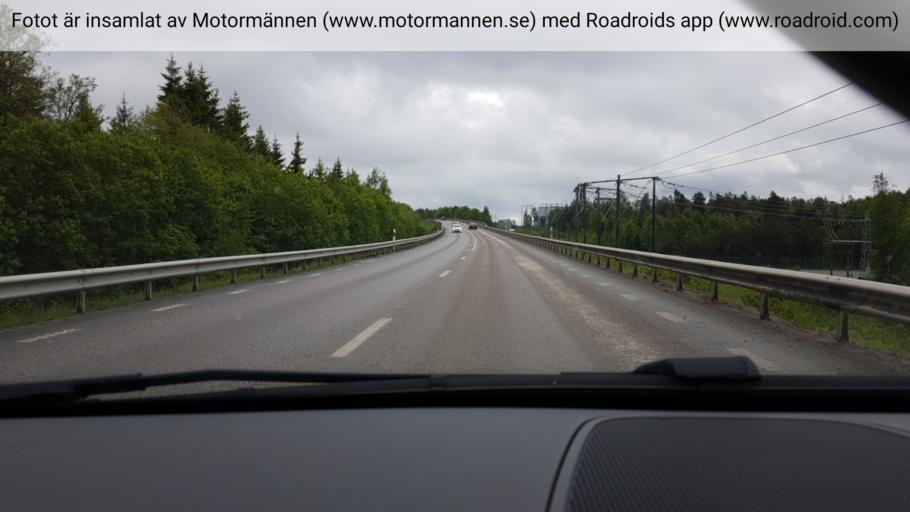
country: SE
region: Stockholm
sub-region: Haninge Kommun
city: Jordbro
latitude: 59.1560
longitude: 18.1218
